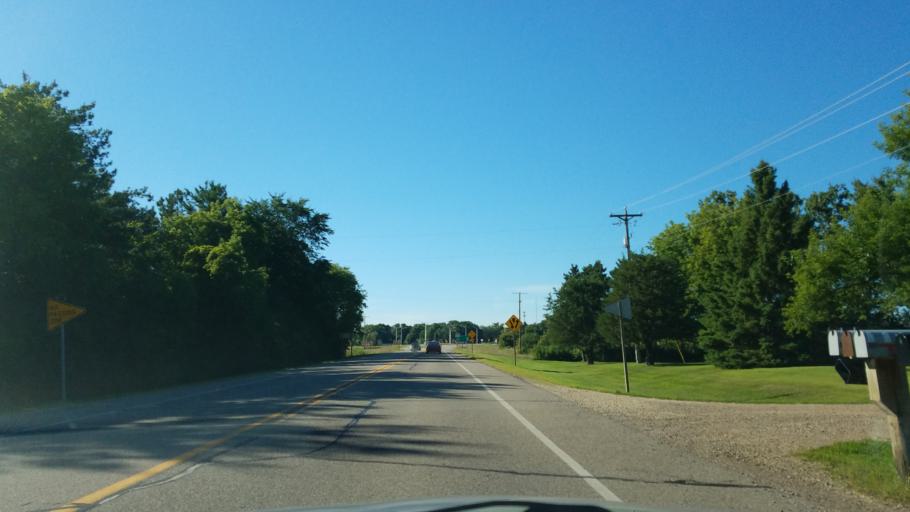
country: US
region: Minnesota
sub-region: Washington County
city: Stillwater
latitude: 45.0523
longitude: -92.7874
